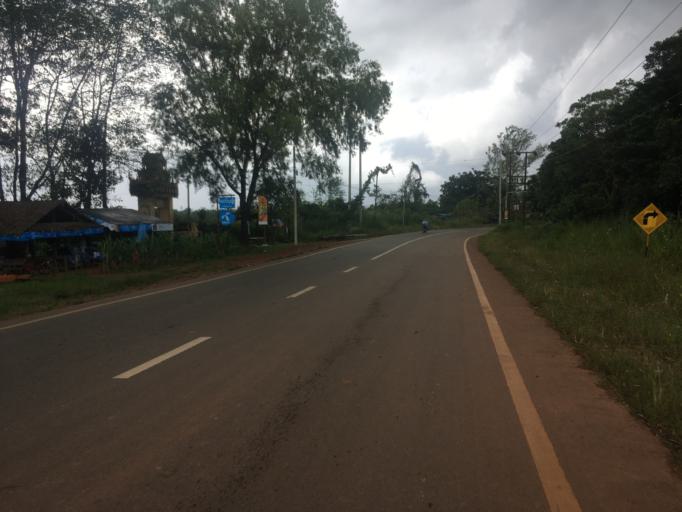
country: MM
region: Mon
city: Mawlamyine
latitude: 16.4554
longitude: 97.6779
